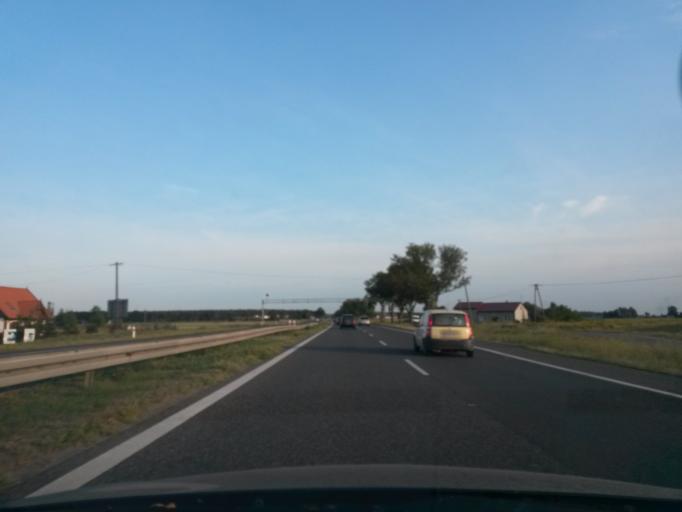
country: PL
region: Masovian Voivodeship
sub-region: Powiat nowodworski
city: Zakroczym
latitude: 52.4699
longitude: 20.5690
